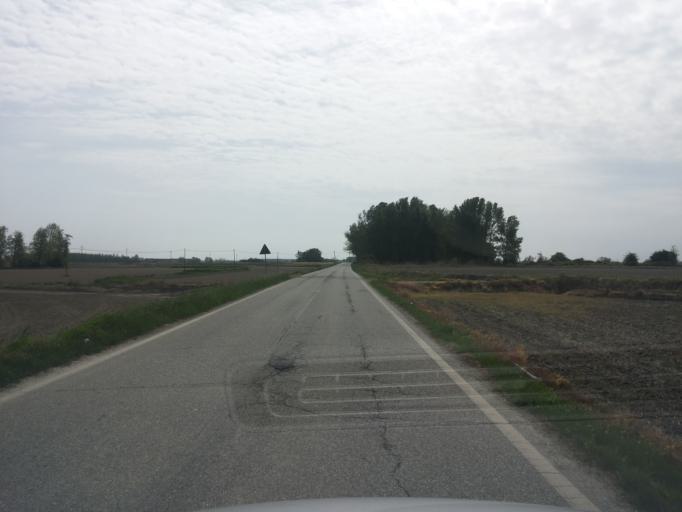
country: IT
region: Piedmont
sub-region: Provincia di Vercelli
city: Caresana
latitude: 45.2118
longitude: 8.5059
